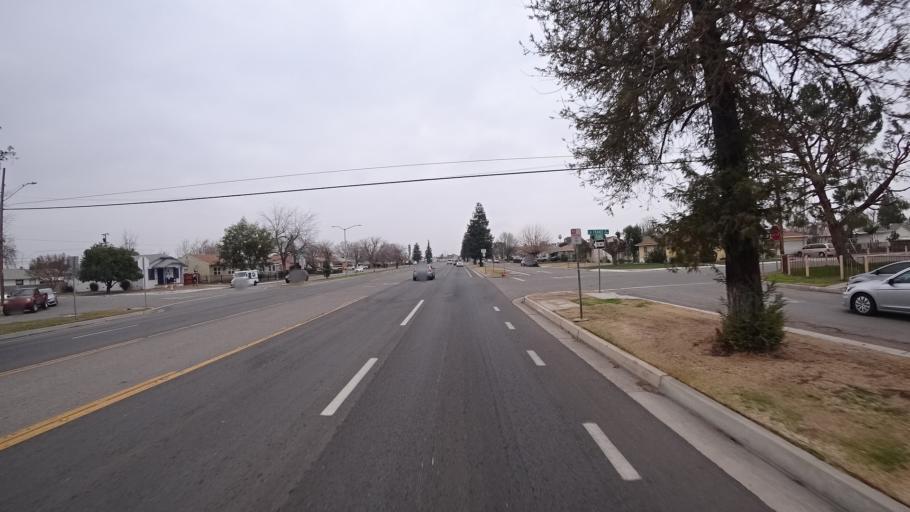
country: US
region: California
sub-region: Kern County
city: Bakersfield
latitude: 35.3433
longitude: -119.0191
